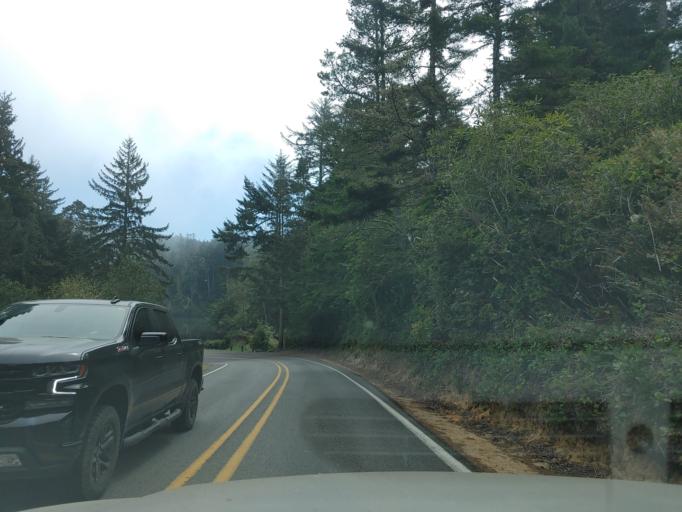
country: US
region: Oregon
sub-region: Coos County
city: Lakeside
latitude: 43.6615
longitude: -124.1986
